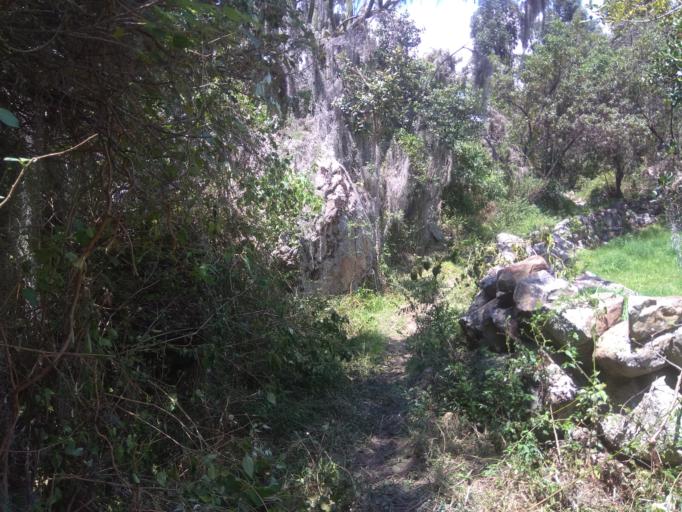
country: CO
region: Boyaca
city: Socha Viejo
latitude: 5.9991
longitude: -72.7137
